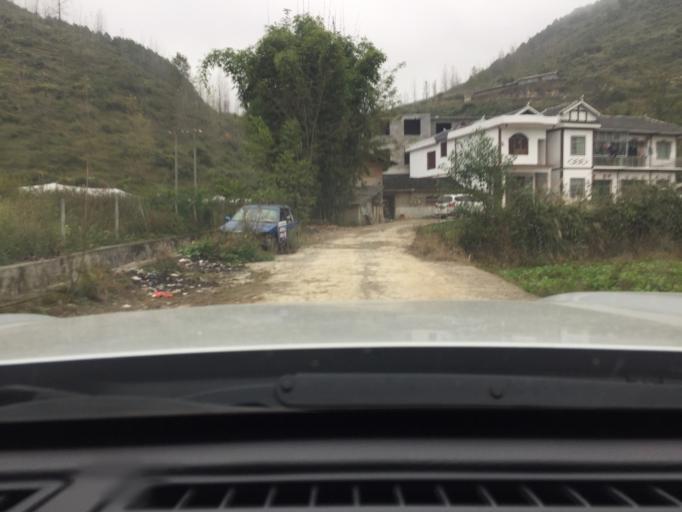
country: CN
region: Guizhou Sheng
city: Jiancha
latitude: 28.1698
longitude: 108.0048
